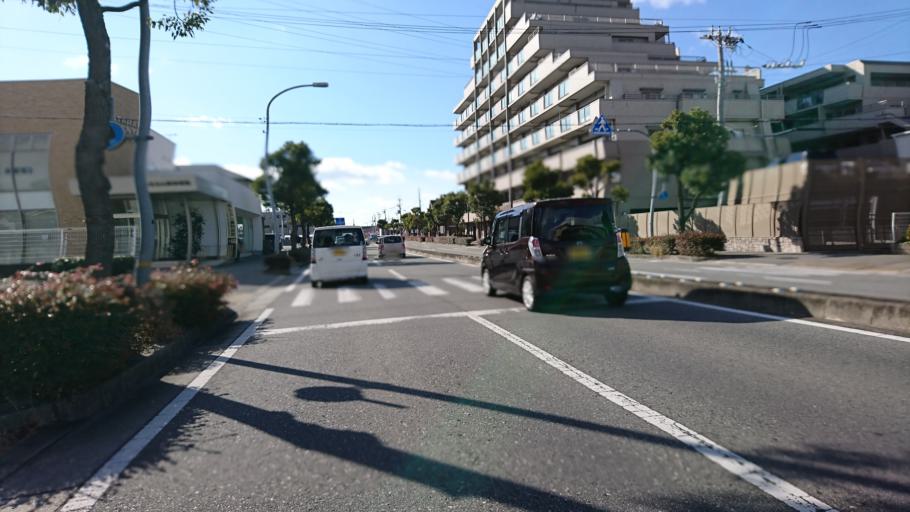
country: JP
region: Hyogo
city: Kakogawacho-honmachi
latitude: 34.7580
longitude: 134.8262
